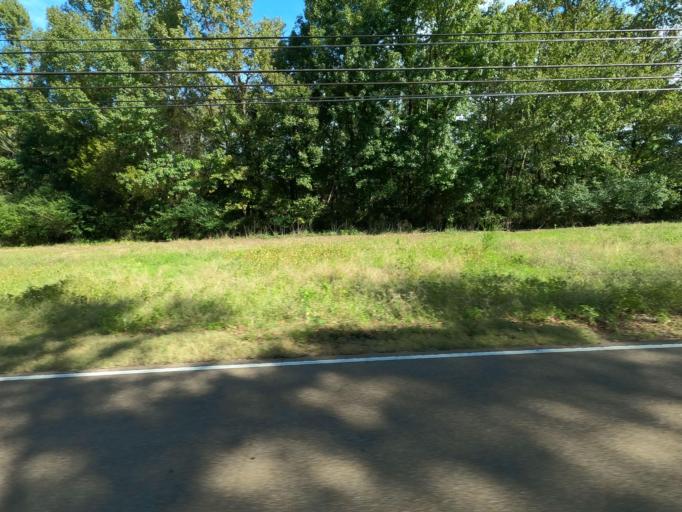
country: US
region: Tennessee
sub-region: Fayette County
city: Hickory Withe
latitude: 35.2293
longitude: -89.6501
